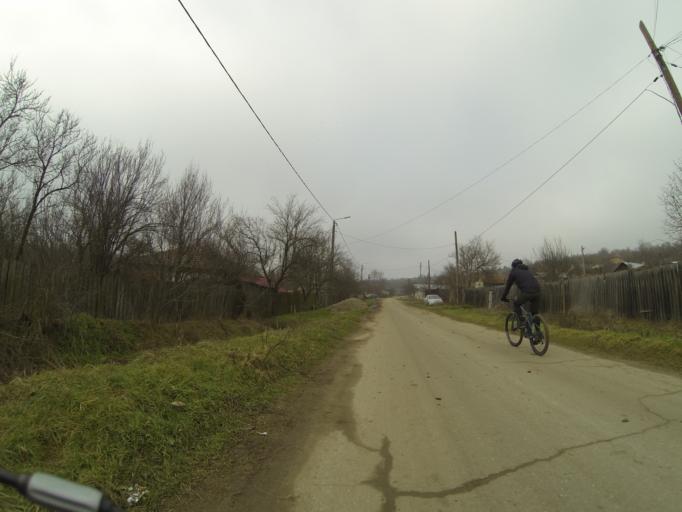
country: RO
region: Mehedinti
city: Padina Mica
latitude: 44.4902
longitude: 23.0104
